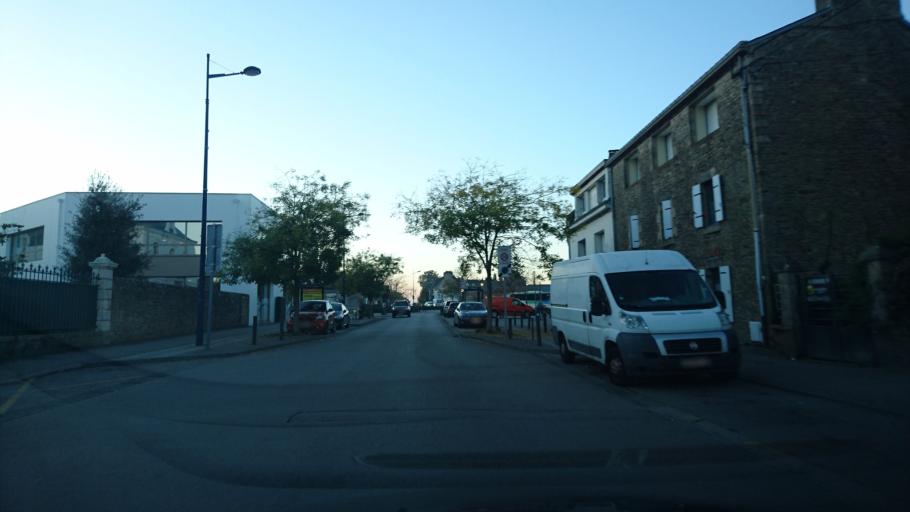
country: FR
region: Brittany
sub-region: Departement du Morbihan
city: Auray
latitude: 47.6699
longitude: -2.9895
